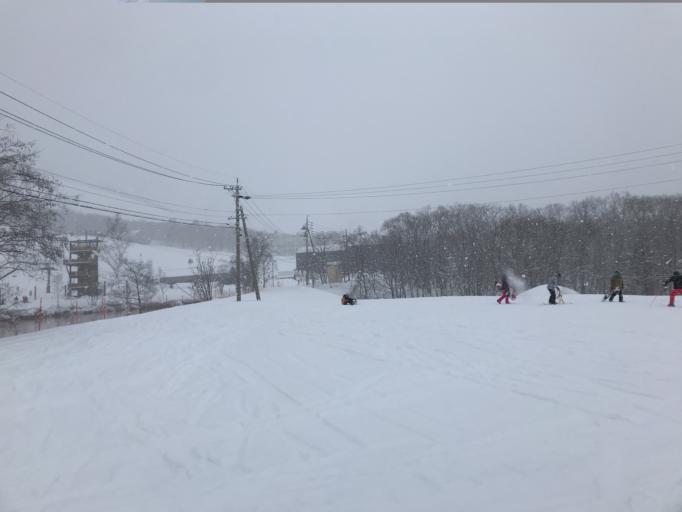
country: JP
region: Nagano
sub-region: Kitaazumi Gun
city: Hakuba
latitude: 36.7524
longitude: 137.8599
